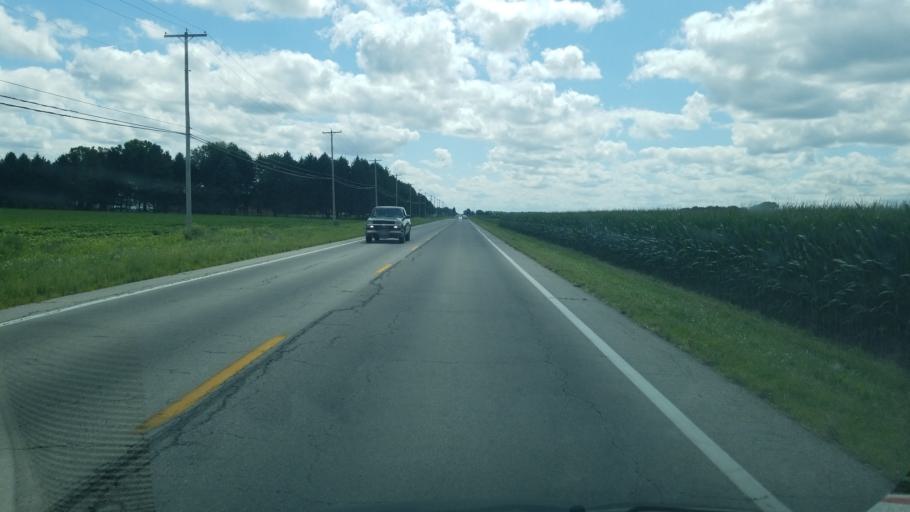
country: US
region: Ohio
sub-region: Henry County
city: Napoleon
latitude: 41.3611
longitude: -84.1201
